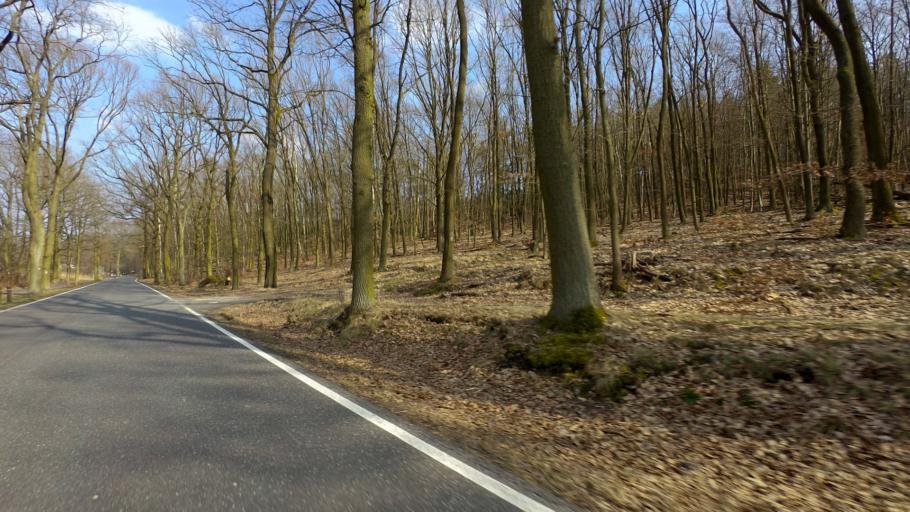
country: DE
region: Brandenburg
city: Werder
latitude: 52.3243
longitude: 12.9581
